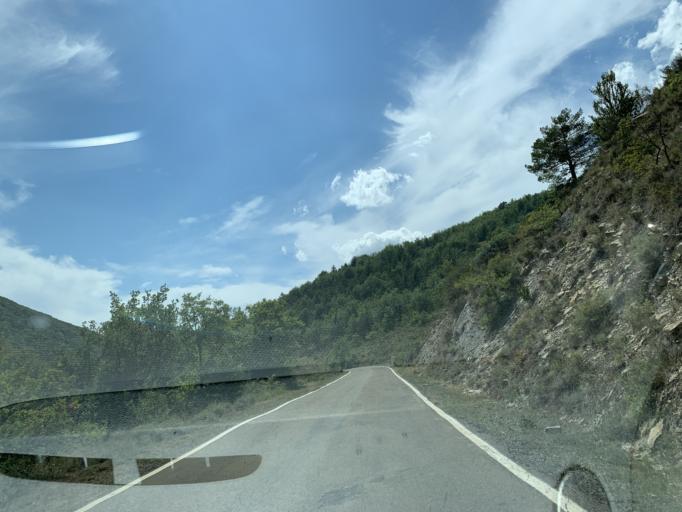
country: ES
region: Aragon
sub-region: Provincia de Huesca
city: Jasa
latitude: 42.6320
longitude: -0.6484
